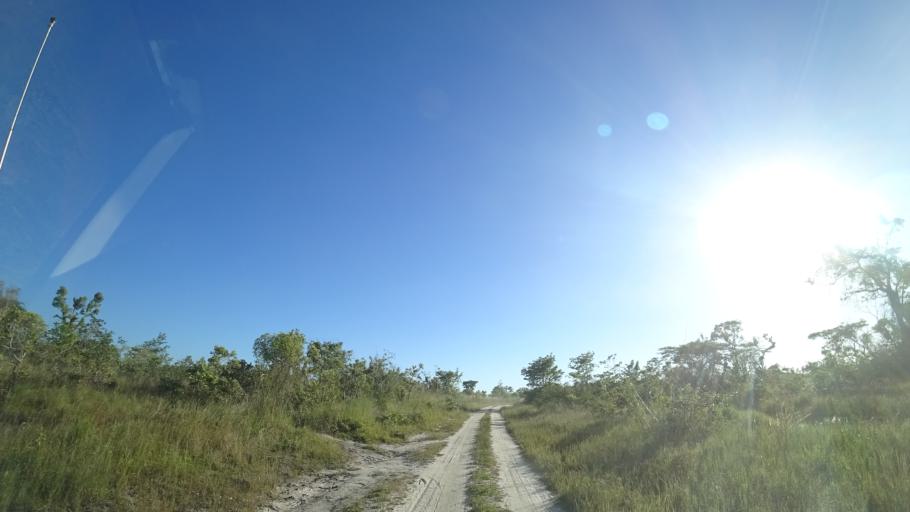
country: MZ
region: Sofala
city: Beira
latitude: -19.5747
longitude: 35.2240
